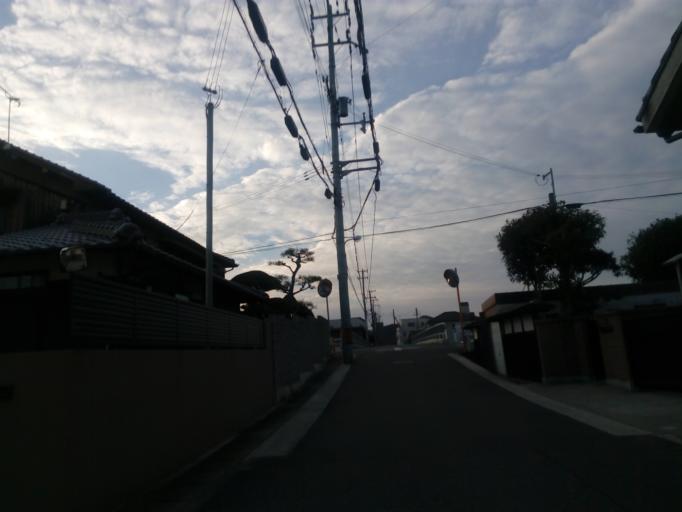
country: JP
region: Hyogo
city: Himeji
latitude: 34.8141
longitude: 134.6716
